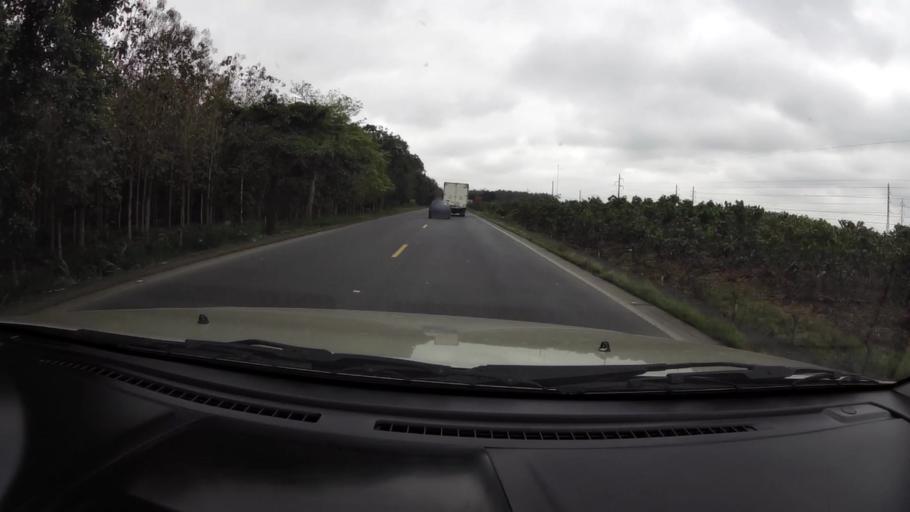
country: EC
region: Guayas
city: Naranjal
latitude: -2.7937
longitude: -79.7054
